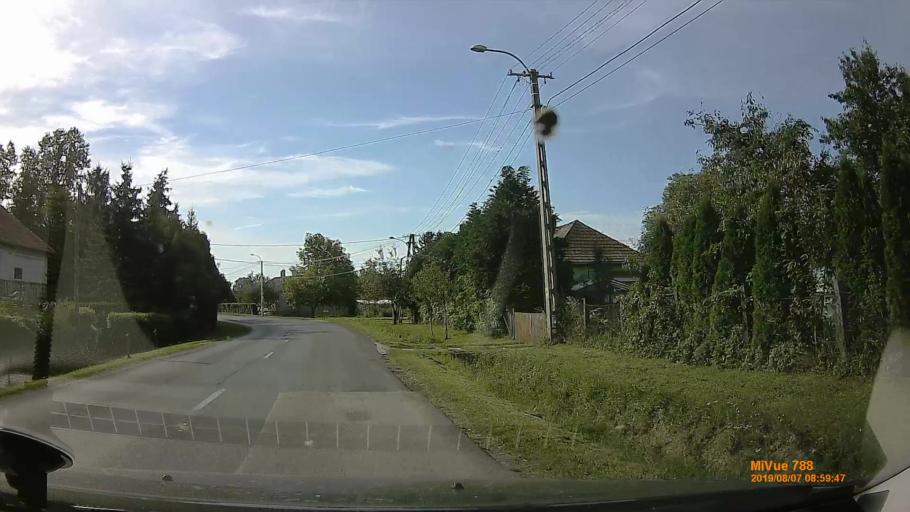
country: HU
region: Zala
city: Pacsa
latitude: 46.7315
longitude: 16.9410
